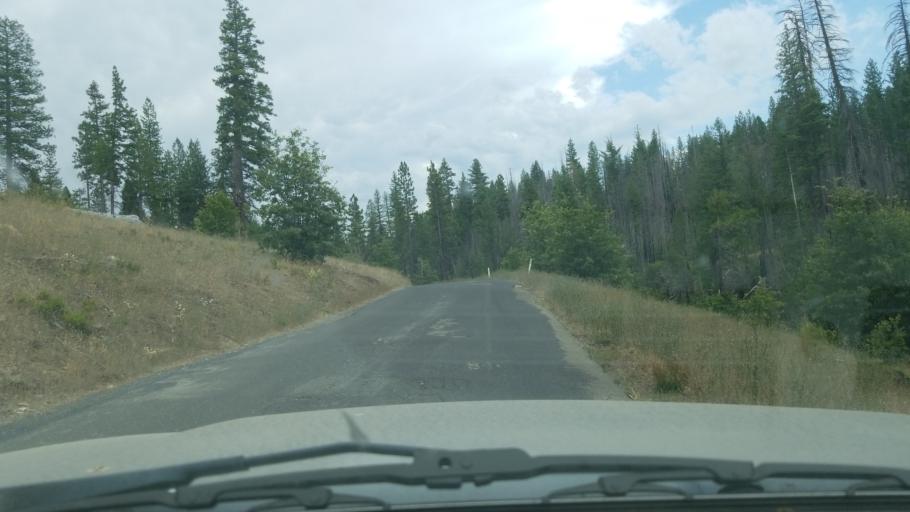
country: US
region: California
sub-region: Mariposa County
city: Yosemite Valley
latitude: 37.8584
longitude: -119.8679
